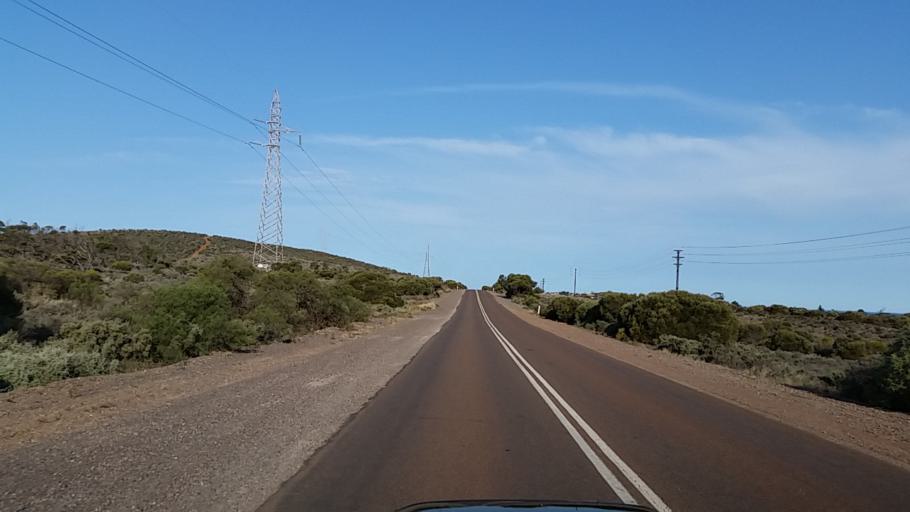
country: AU
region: South Australia
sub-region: Whyalla
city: Whyalla
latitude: -33.0075
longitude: 137.5333
